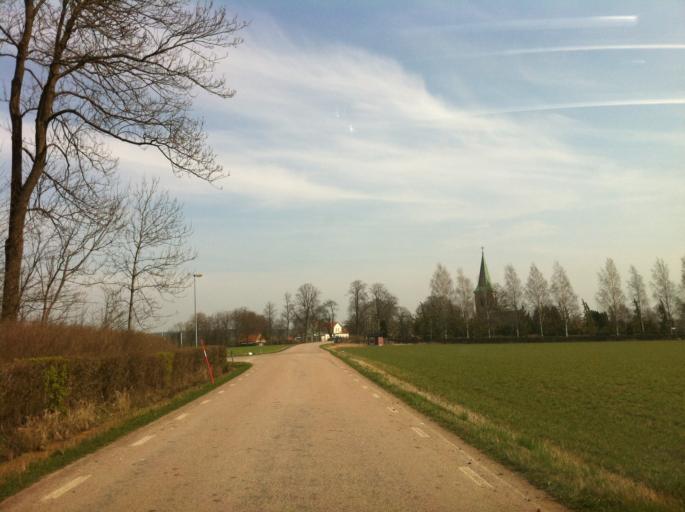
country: SE
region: Skane
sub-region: Svalovs Kommun
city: Svaloev
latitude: 55.9241
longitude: 13.0987
